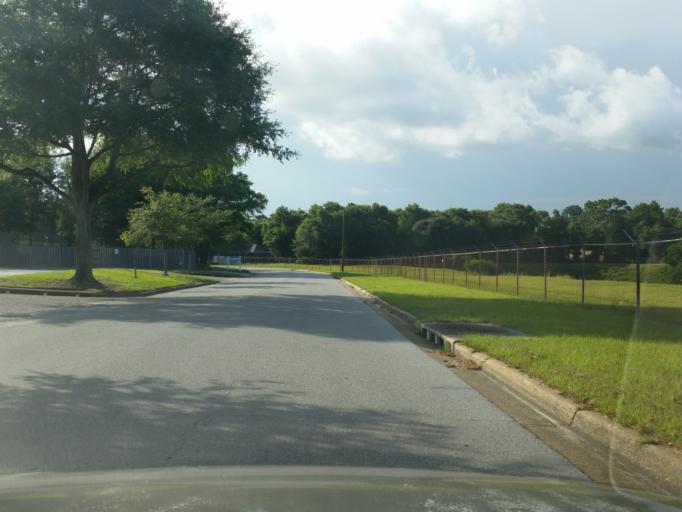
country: US
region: Florida
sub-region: Escambia County
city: Goulding
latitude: 30.4694
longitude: -87.2029
